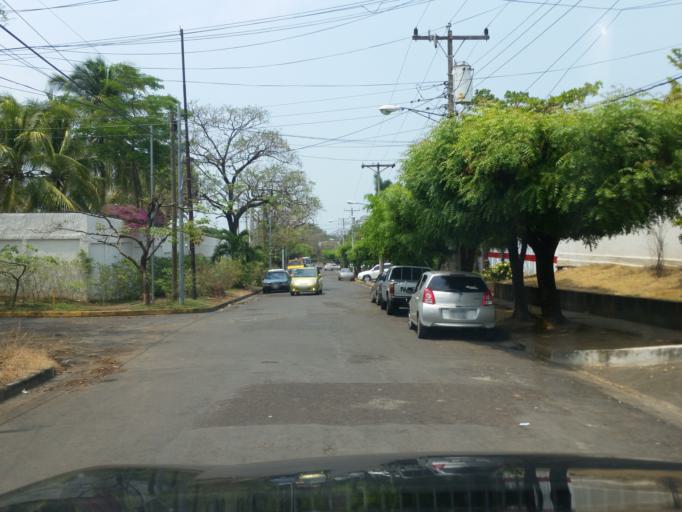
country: NI
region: Managua
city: Managua
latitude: 12.1200
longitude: -86.2675
